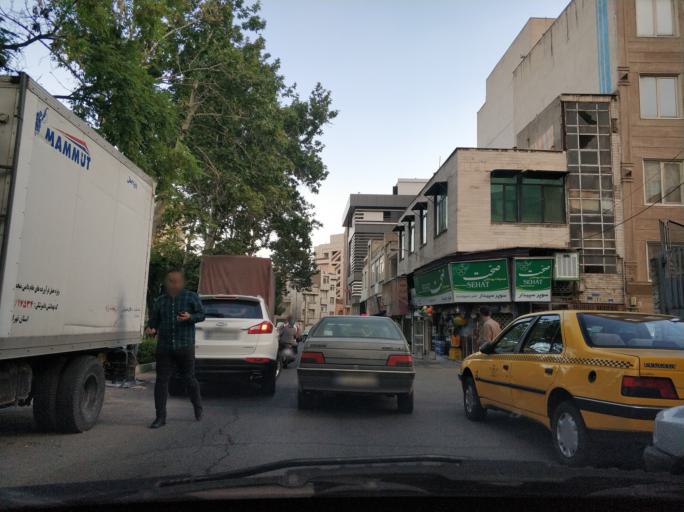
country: IR
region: Tehran
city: Tehran
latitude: 35.7176
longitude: 51.4772
